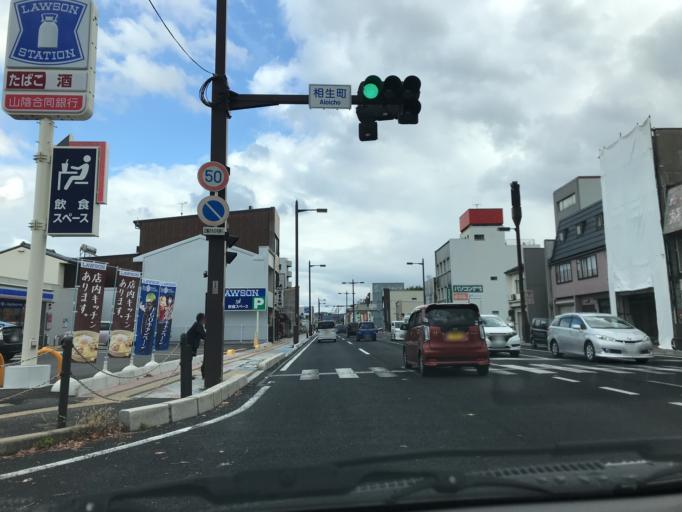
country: JP
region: Shimane
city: Matsue-shi
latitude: 35.4590
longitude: 133.0606
